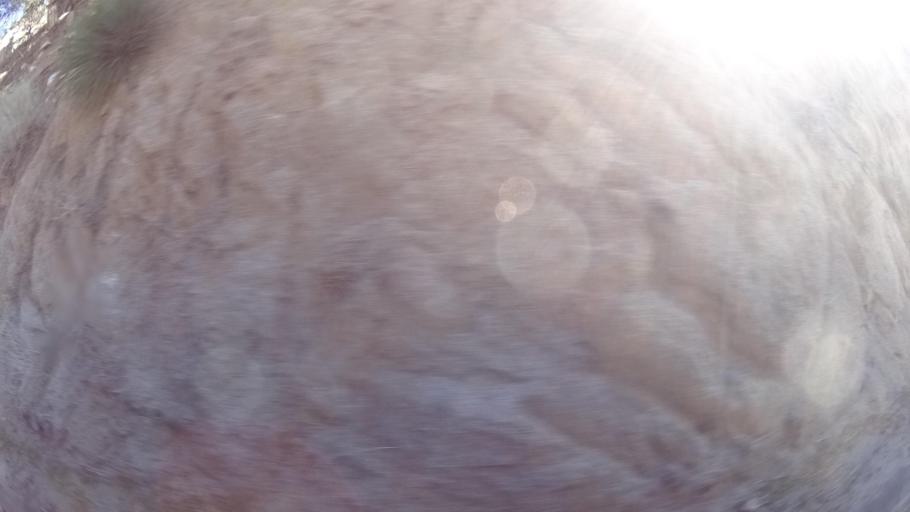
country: US
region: California
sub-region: Kern County
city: Bodfish
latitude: 35.5703
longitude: -118.5664
